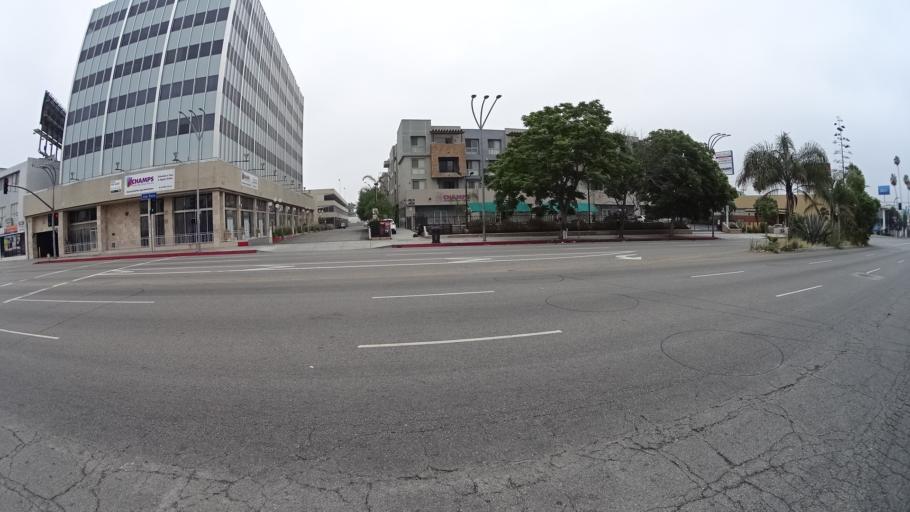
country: US
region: California
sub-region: Los Angeles County
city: Van Nuys
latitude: 34.1949
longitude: -118.4489
